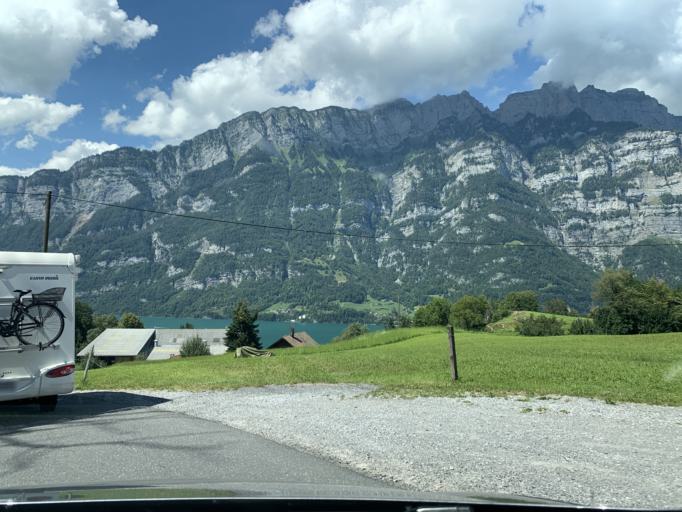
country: CH
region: Saint Gallen
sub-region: Wahlkreis Sarganserland
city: Quarten
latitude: 47.1097
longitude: 9.2140
